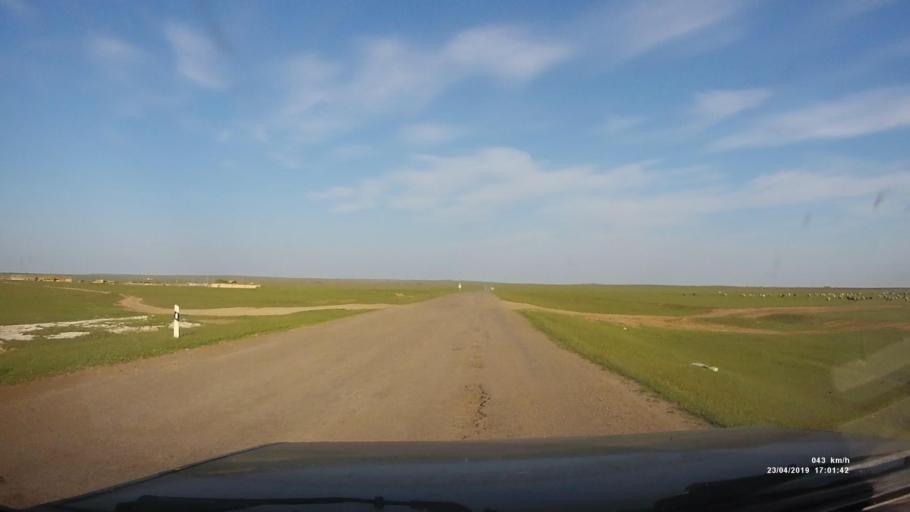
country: RU
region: Kalmykiya
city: Priyutnoye
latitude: 46.2946
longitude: 43.4090
